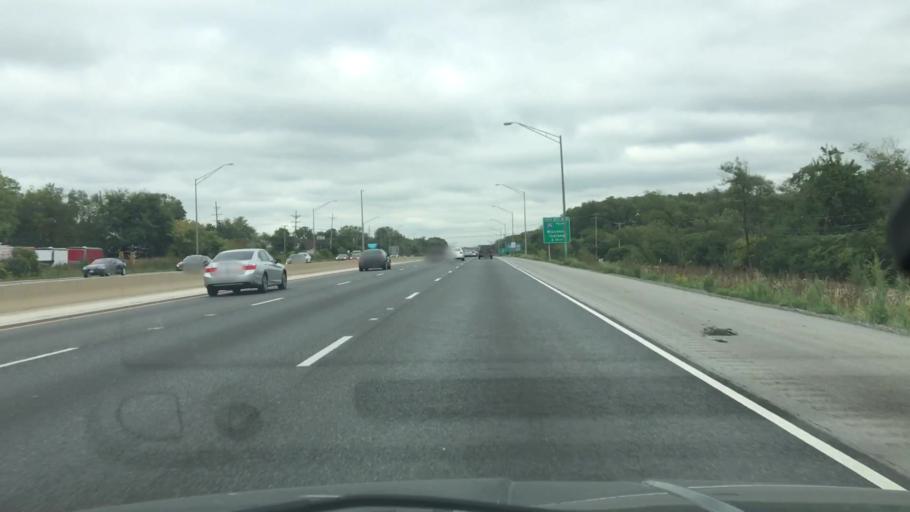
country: US
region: Illinois
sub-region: DuPage County
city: Darien
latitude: 41.7344
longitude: -87.9639
